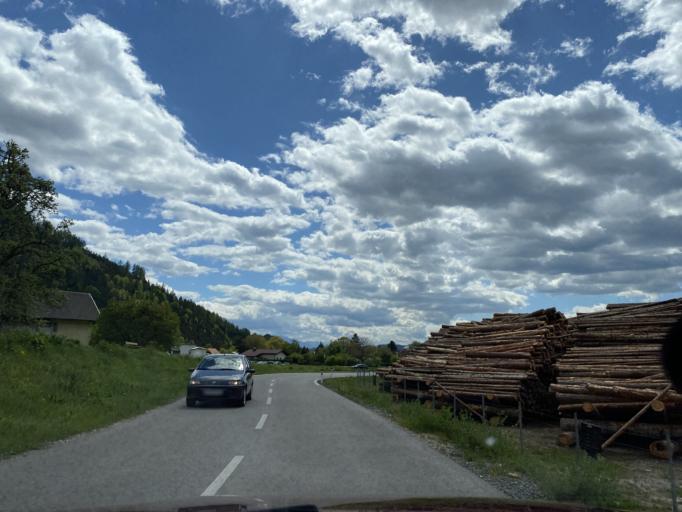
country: AT
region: Carinthia
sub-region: Politischer Bezirk Wolfsberg
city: Wolfsberg
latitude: 46.8585
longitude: 14.8515
